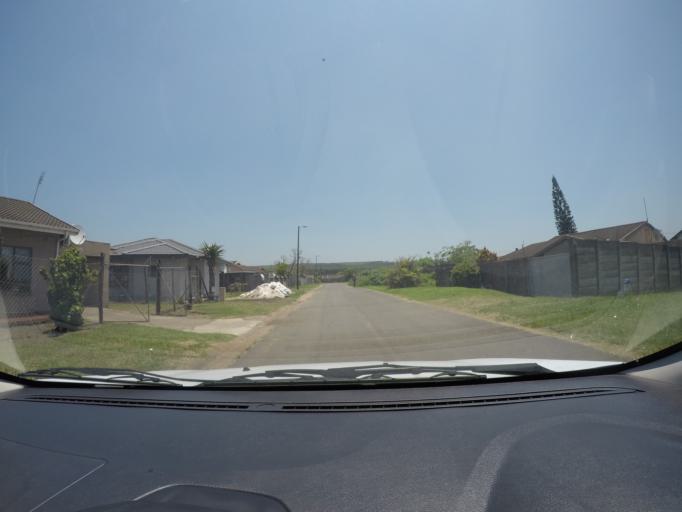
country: ZA
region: KwaZulu-Natal
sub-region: uThungulu District Municipality
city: eSikhawini
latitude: -28.8760
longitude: 31.8980
